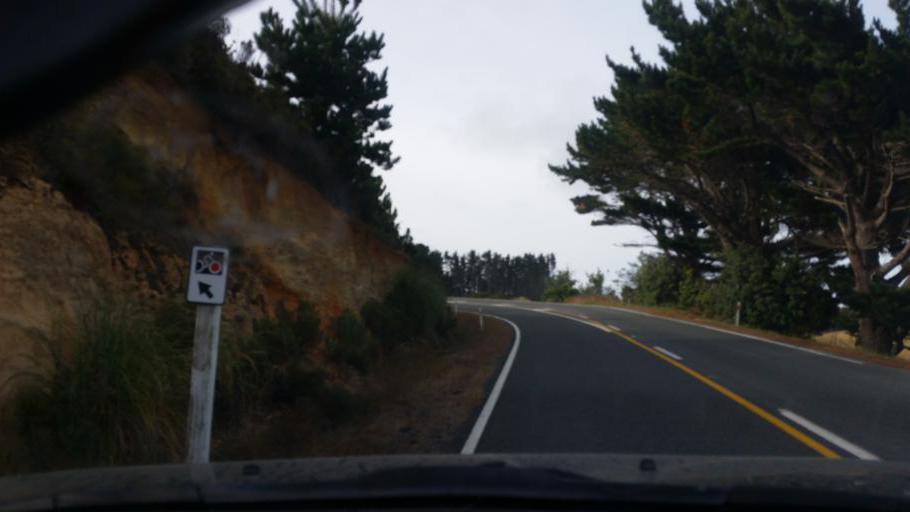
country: NZ
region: Northland
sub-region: Kaipara District
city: Dargaville
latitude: -36.2147
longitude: 174.0312
